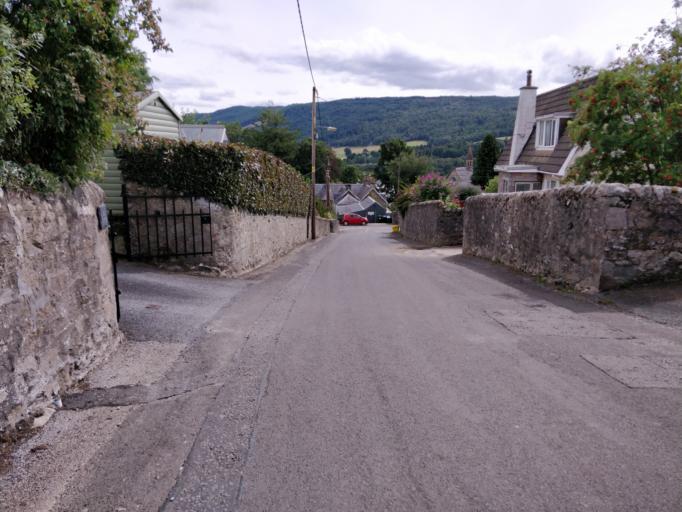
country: GB
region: Scotland
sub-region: Perth and Kinross
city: Pitlochry
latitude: 56.7052
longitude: -3.7285
